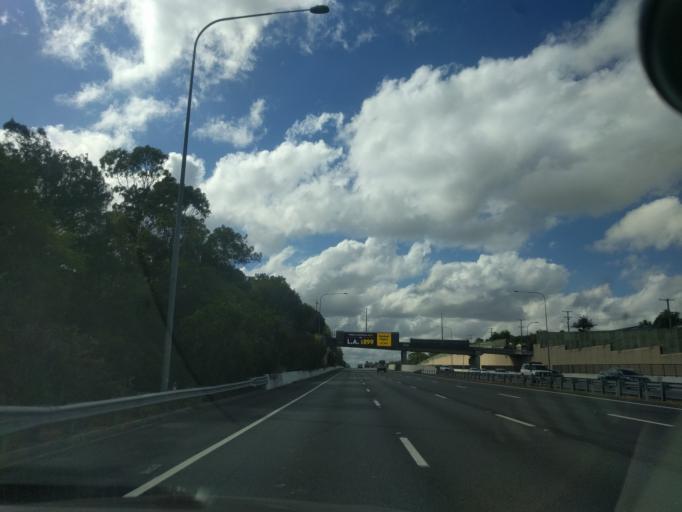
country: AU
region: Queensland
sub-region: Brisbane
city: Nathan
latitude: -27.5571
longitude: 153.0726
